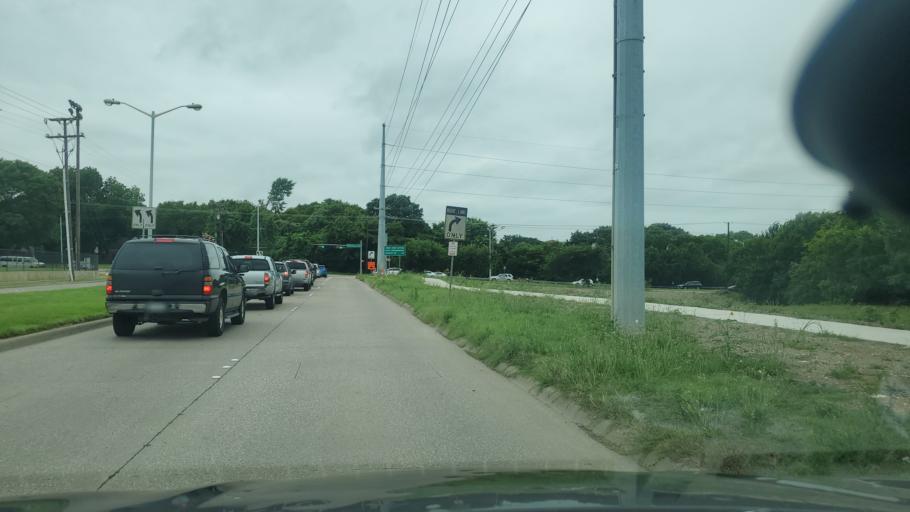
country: US
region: Texas
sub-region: Dallas County
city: Garland
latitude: 32.9547
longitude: -96.6555
